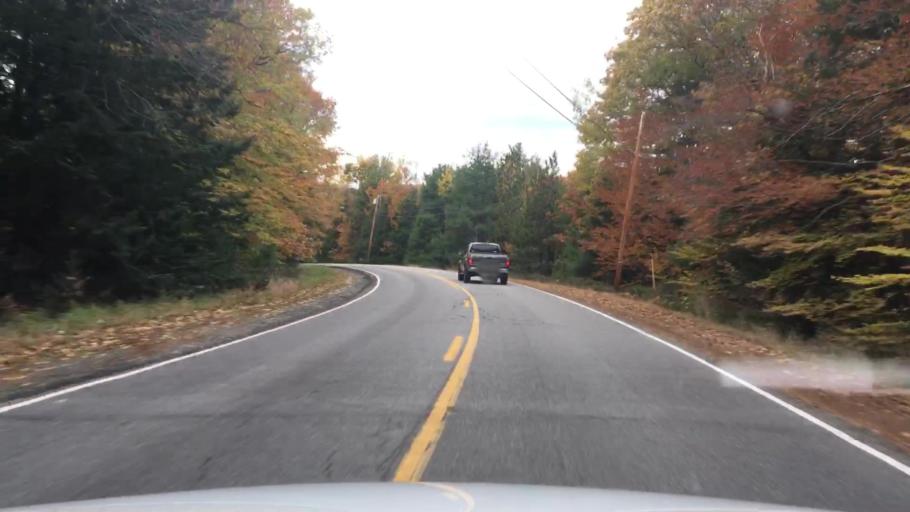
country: US
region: Maine
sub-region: Androscoggin County
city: Sabattus
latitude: 44.1360
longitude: -70.0042
